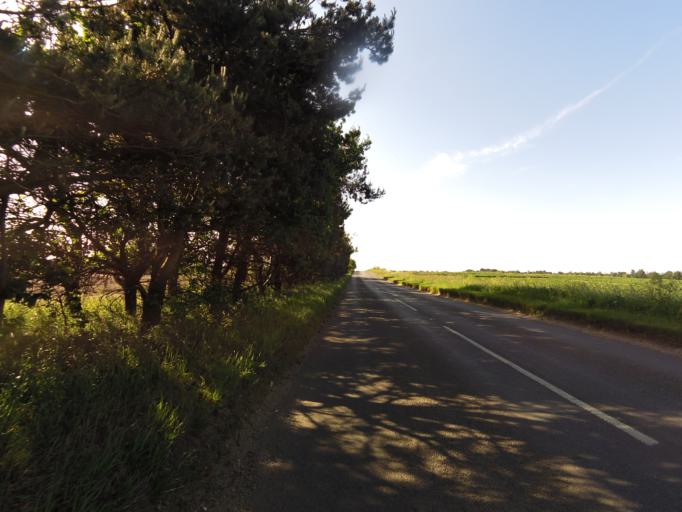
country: GB
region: England
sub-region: Suffolk
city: Woodbridge
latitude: 52.0840
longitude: 1.3589
